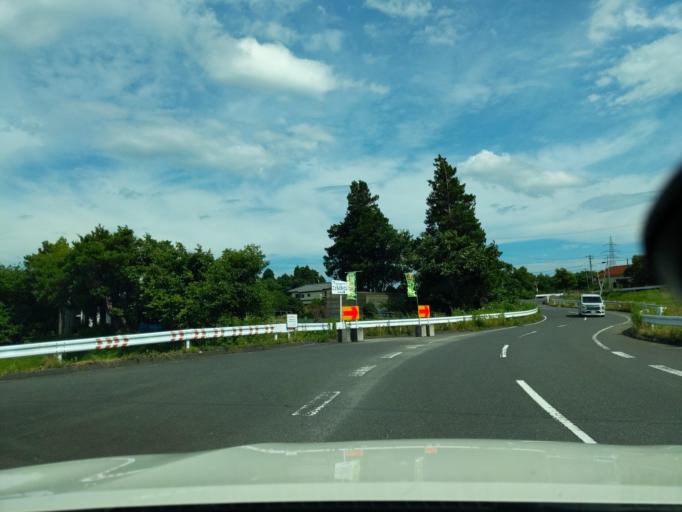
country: JP
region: Fukushima
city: Koriyama
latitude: 37.4383
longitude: 140.3945
